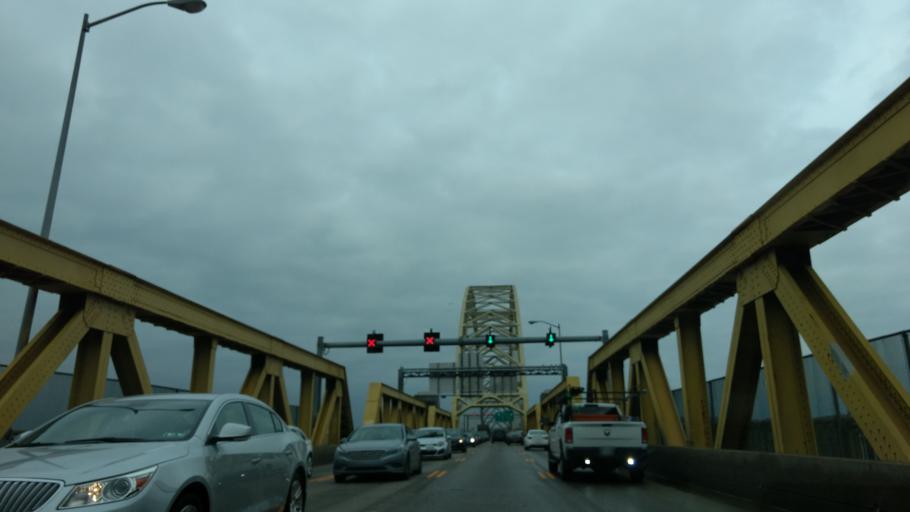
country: US
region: Pennsylvania
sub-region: Allegheny County
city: Pittsburgh
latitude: 40.4445
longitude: -80.0280
